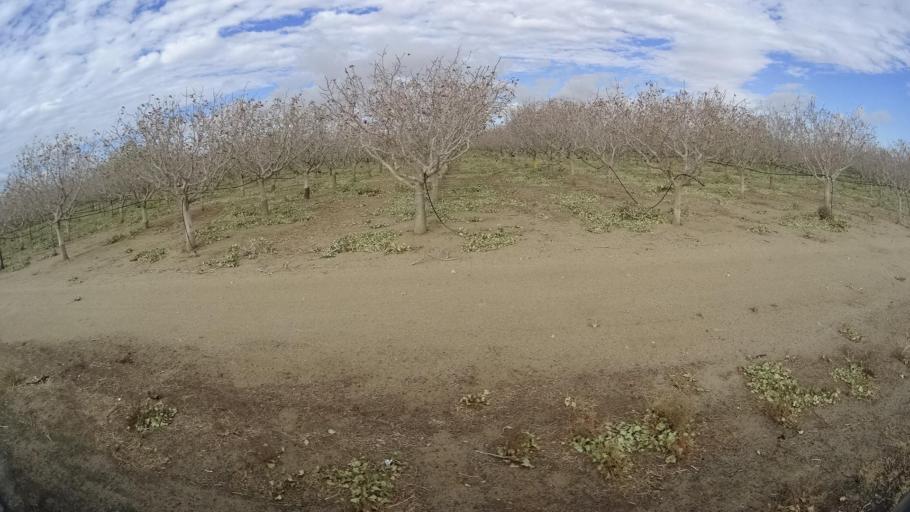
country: US
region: California
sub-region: Kern County
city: Rosamond
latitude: 34.8200
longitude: -118.3139
